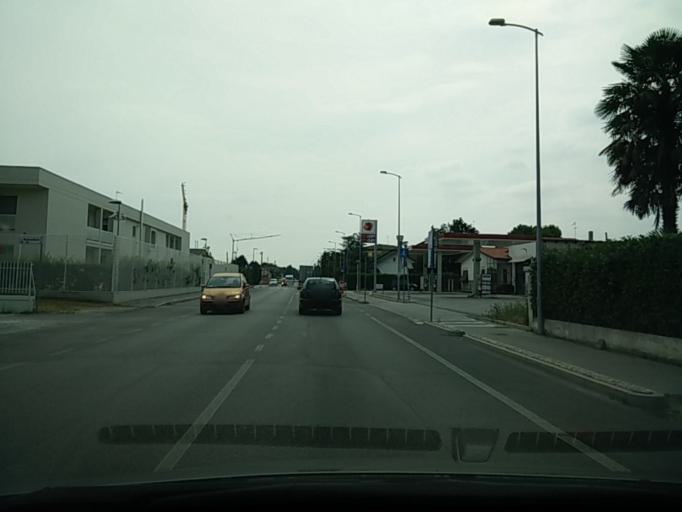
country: IT
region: Veneto
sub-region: Provincia di Treviso
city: Casale sul Sile
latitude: 45.6026
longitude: 12.3309
